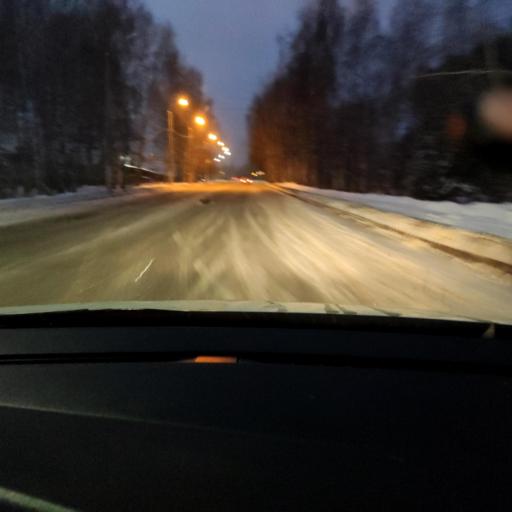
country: RU
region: Tatarstan
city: Aysha
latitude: 55.8714
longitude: 48.5788
